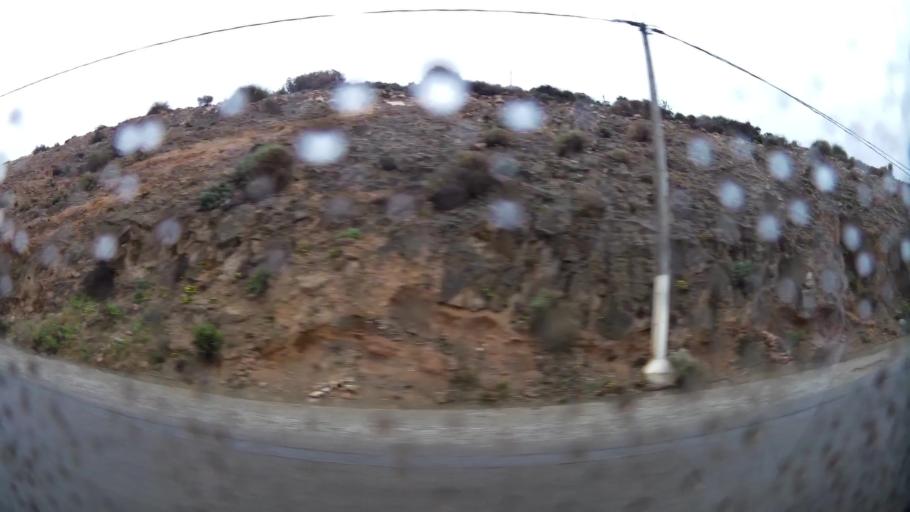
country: MA
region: Taza-Al Hoceima-Taounate
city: Tirhanimine
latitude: 35.2437
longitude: -3.9639
